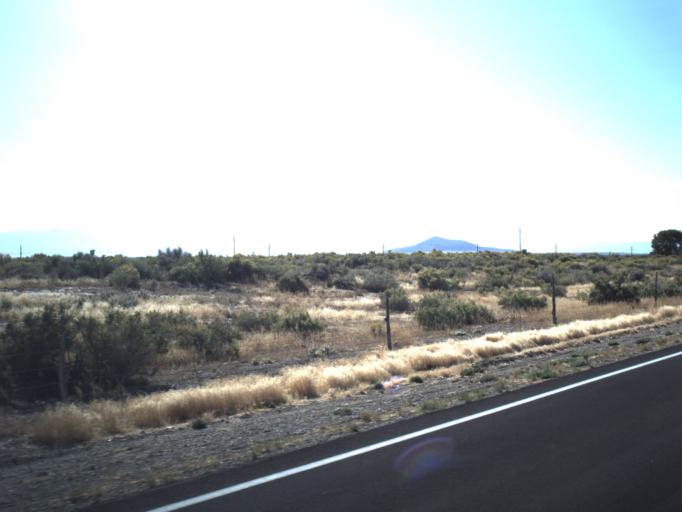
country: US
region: Utah
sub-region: Millard County
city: Delta
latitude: 39.2611
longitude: -112.6532
